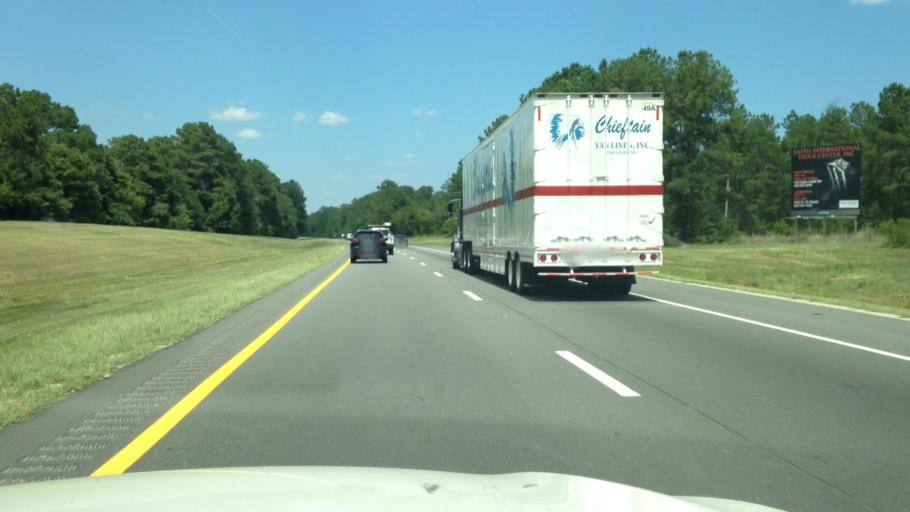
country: US
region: North Carolina
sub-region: Cumberland County
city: Hope Mills
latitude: 34.9428
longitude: -78.9122
